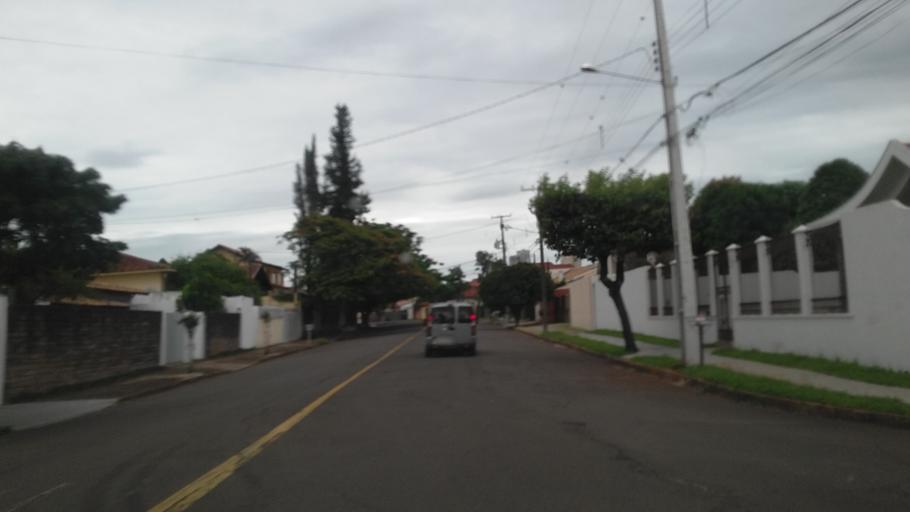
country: BR
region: Parana
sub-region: Londrina
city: Londrina
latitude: -23.3158
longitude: -51.1794
